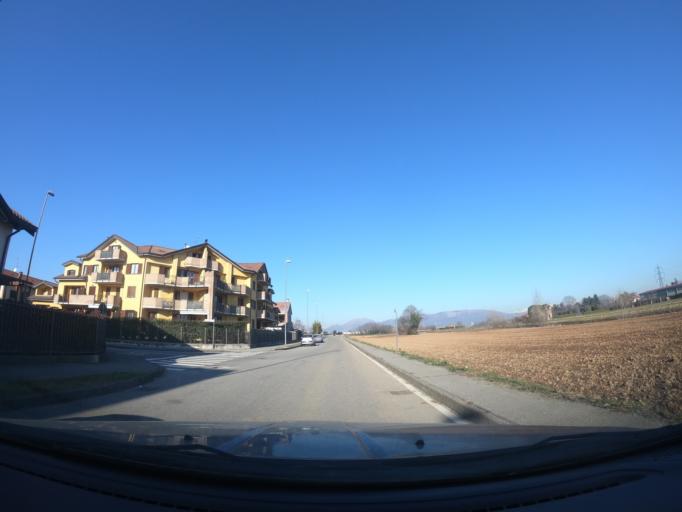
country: IT
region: Lombardy
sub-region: Provincia di Monza e Brianza
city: Sulbiate
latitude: 45.6383
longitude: 9.4311
